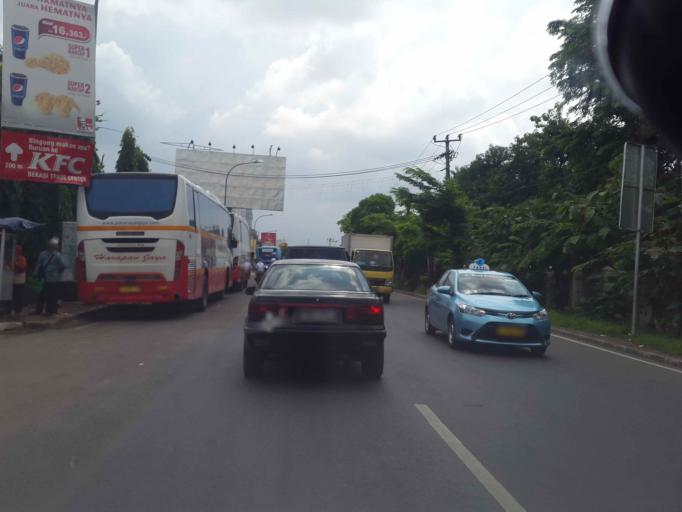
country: ID
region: West Java
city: Bekasi
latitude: -6.2548
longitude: 107.0222
